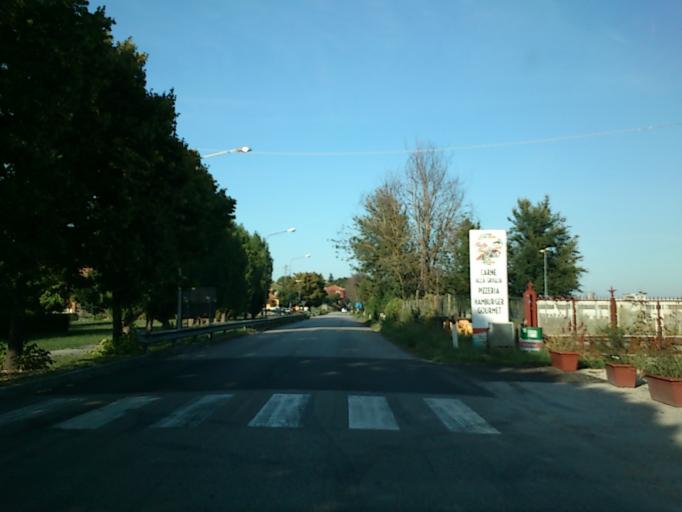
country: IT
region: The Marches
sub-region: Provincia di Pesaro e Urbino
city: Montefelcino
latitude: 43.7142
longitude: 12.8566
